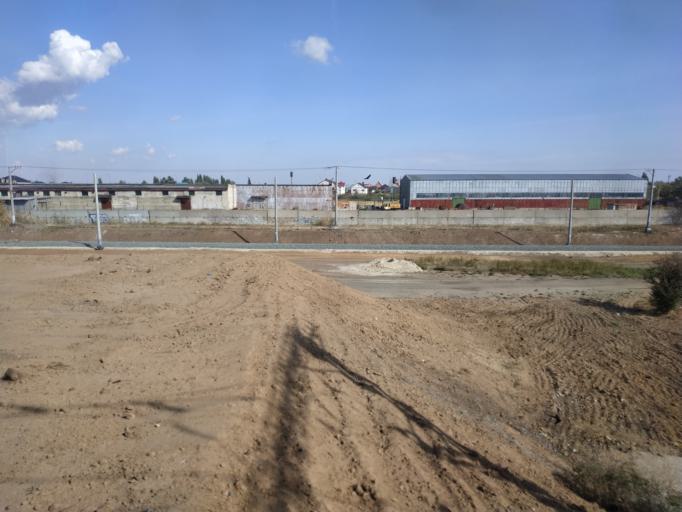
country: RU
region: Volgograd
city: Gumrak
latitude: 48.7717
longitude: 44.3872
